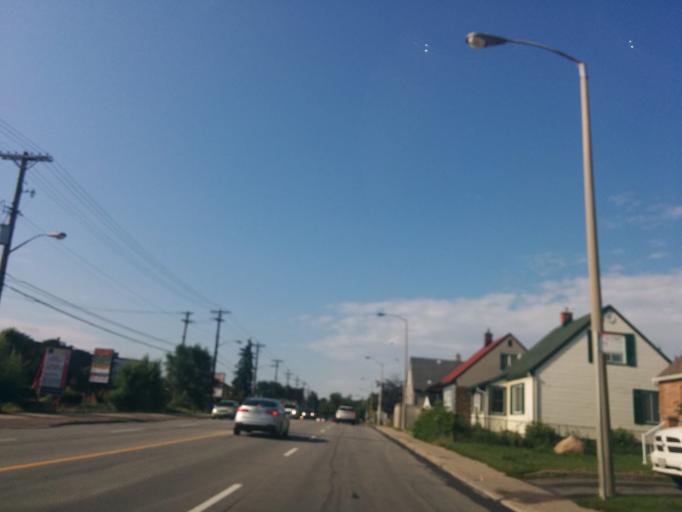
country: CA
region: Ontario
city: Ottawa
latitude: 45.3843
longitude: -75.7325
